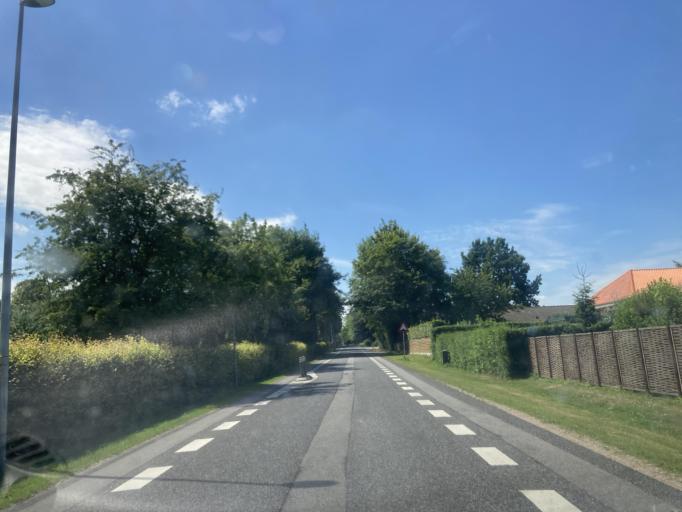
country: DK
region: Zealand
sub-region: Solrod Kommune
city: Solrod
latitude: 55.5234
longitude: 12.1634
